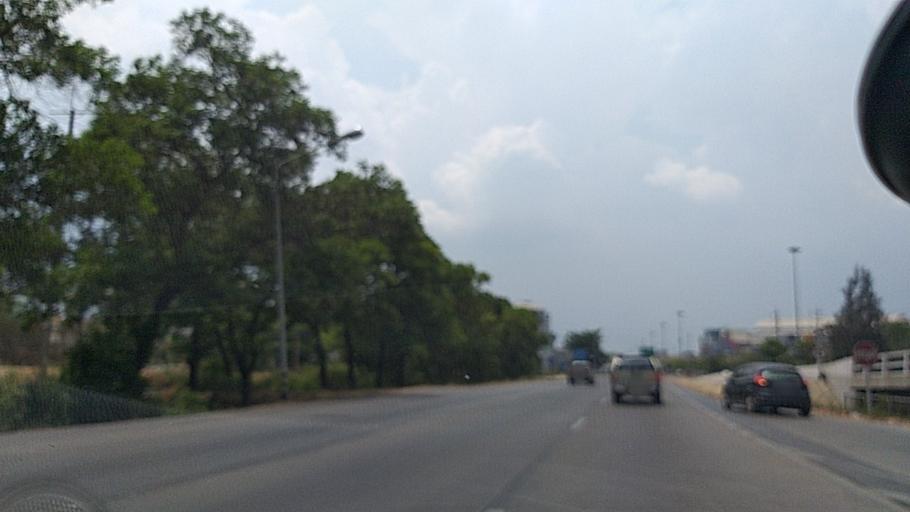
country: TH
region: Phra Nakhon Si Ayutthaya
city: Phra Nakhon Si Ayutthaya
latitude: 14.3417
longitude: 100.6114
